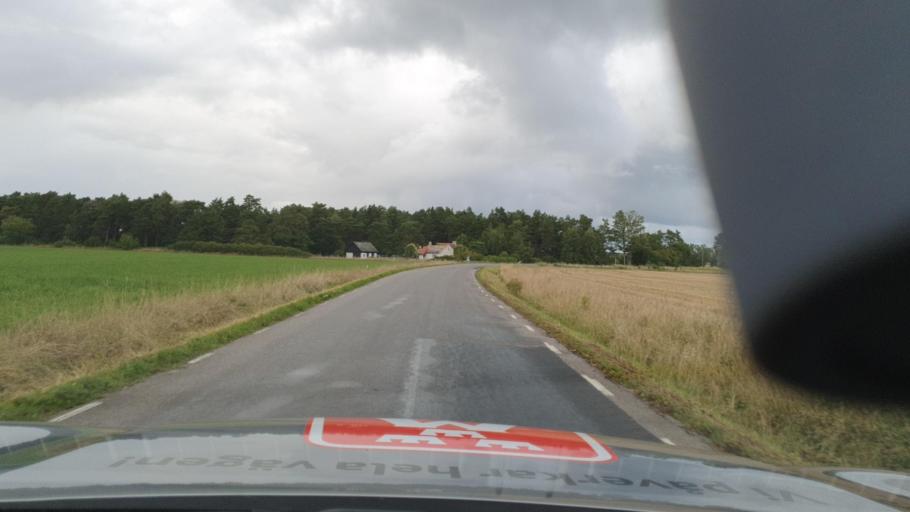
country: SE
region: Gotland
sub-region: Gotland
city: Klintehamn
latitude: 57.4990
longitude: 18.1964
